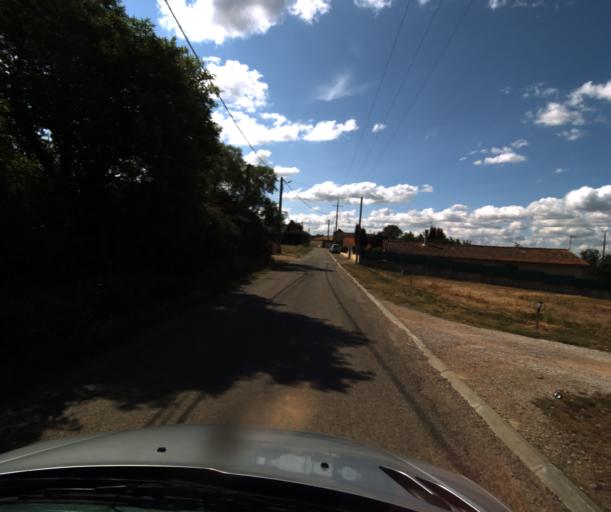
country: FR
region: Midi-Pyrenees
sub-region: Departement du Tarn-et-Garonne
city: Campsas
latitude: 43.8931
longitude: 1.2740
